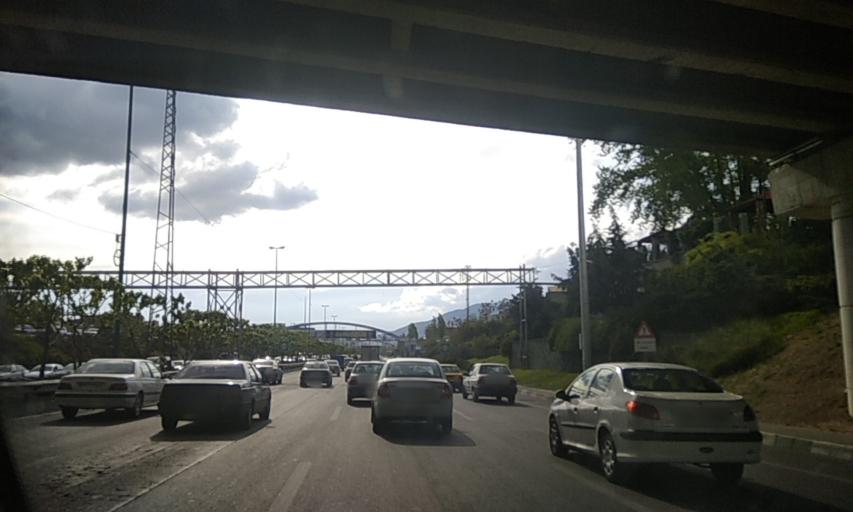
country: IR
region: Tehran
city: Tehran
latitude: 35.7540
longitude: 51.2789
